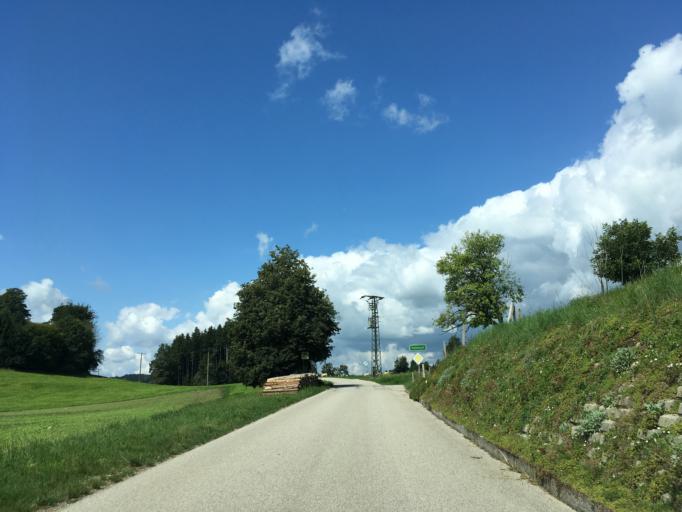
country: DE
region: Bavaria
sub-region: Upper Bavaria
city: Pittenhart
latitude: 47.9736
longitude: 12.3623
